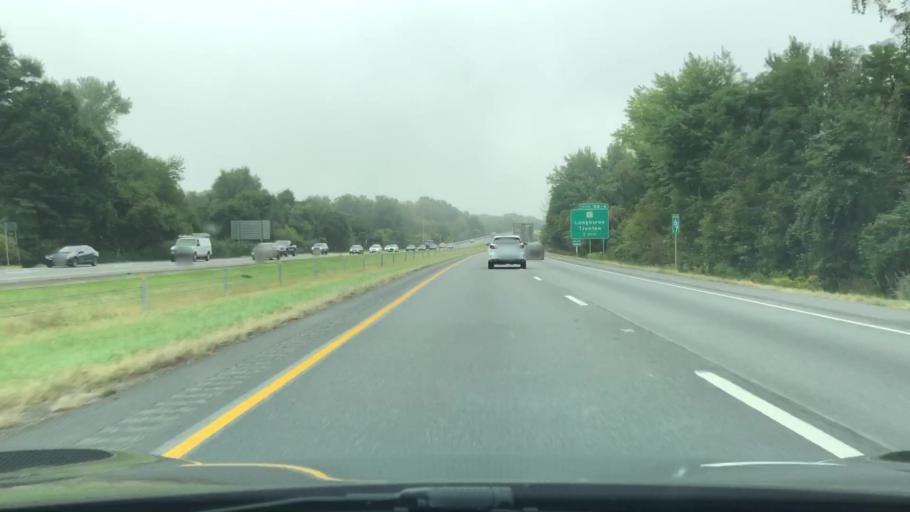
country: US
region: Pennsylvania
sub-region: Bucks County
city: Woodside
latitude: 40.2111
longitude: -74.8763
